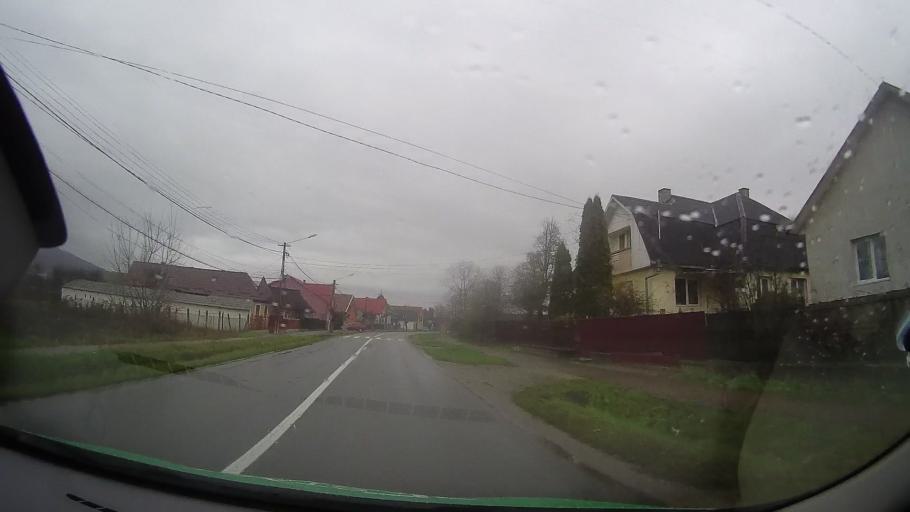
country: RO
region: Bistrita-Nasaud
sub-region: Municipiul Bistrita
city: Viisoara
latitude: 47.0765
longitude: 24.4366
